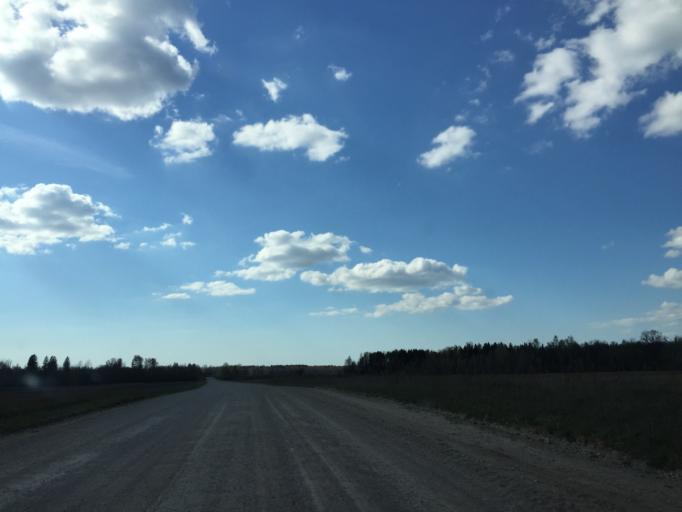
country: LV
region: Krimulda
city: Ragana
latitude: 57.3375
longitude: 24.6362
